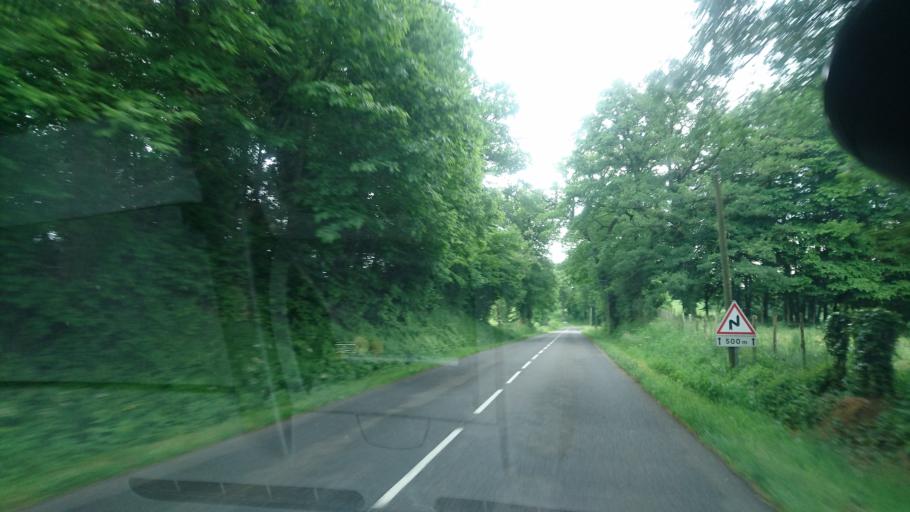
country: FR
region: Limousin
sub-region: Departement de la Haute-Vienne
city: Saint-Germain-les-Belles
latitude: 45.5954
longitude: 1.4784
